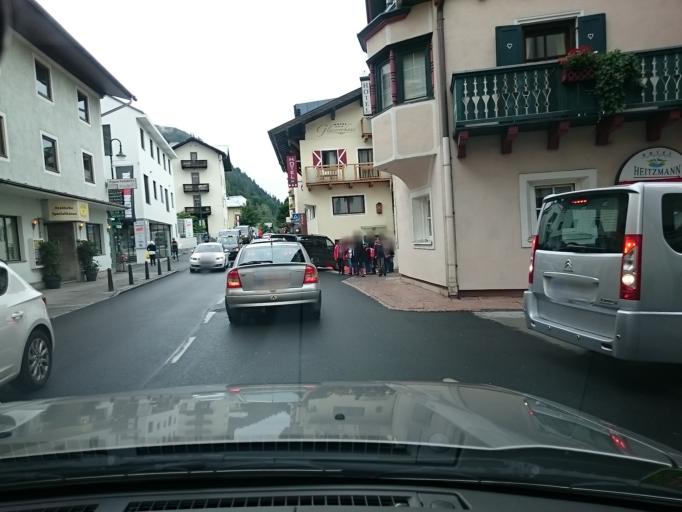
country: AT
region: Salzburg
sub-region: Politischer Bezirk Zell am See
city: Zell am See
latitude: 47.3239
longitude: 12.7966
